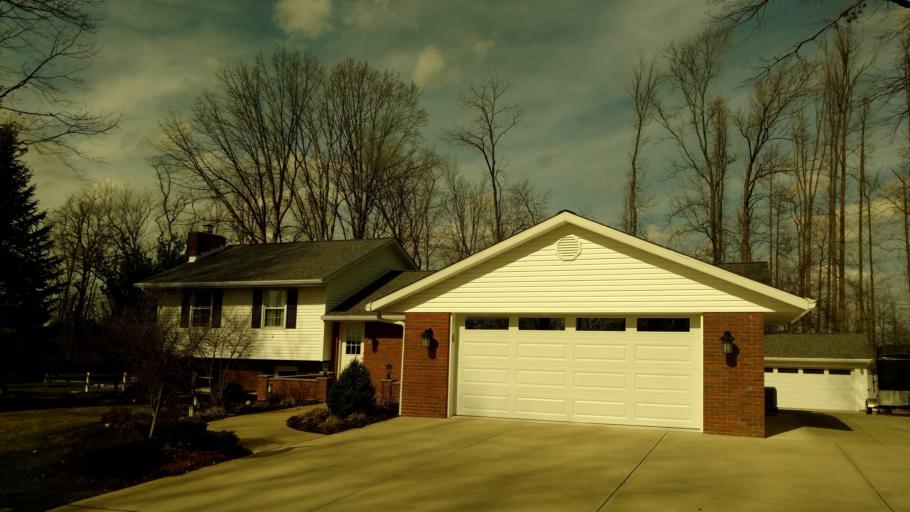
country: US
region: Ohio
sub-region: Knox County
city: Mount Vernon
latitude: 40.4062
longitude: -82.4530
